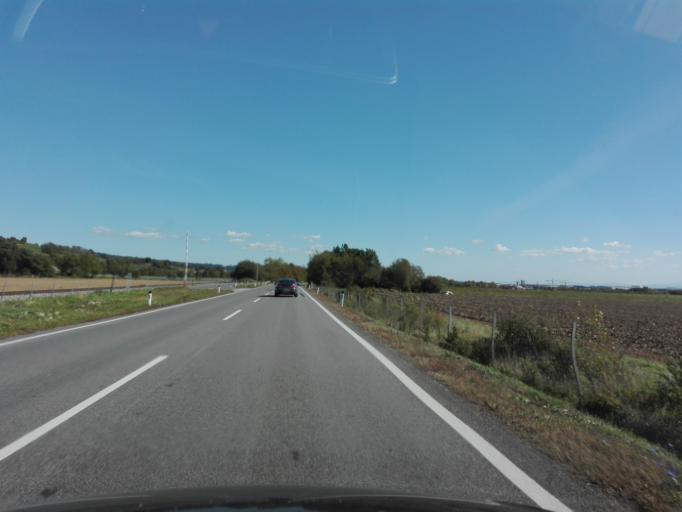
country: AT
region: Upper Austria
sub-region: Politischer Bezirk Perg
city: Perg
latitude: 48.2499
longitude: 14.5975
